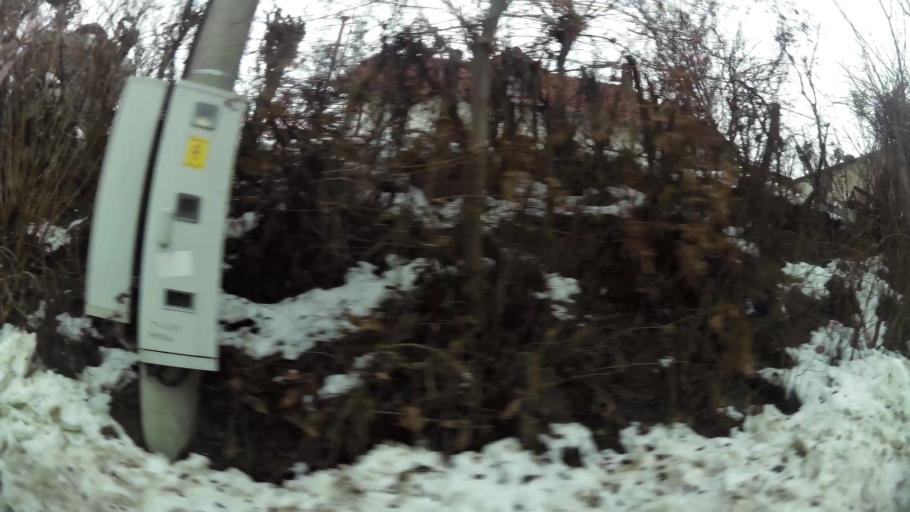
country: RS
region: Central Serbia
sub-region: Belgrade
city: Zvezdara
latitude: 44.7509
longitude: 20.5257
